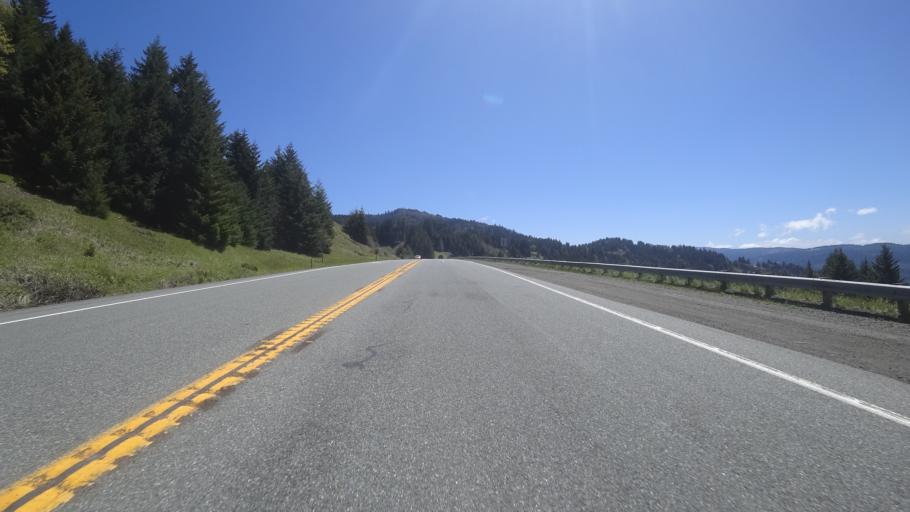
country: US
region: California
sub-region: Humboldt County
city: Willow Creek
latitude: 40.8987
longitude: -123.7753
